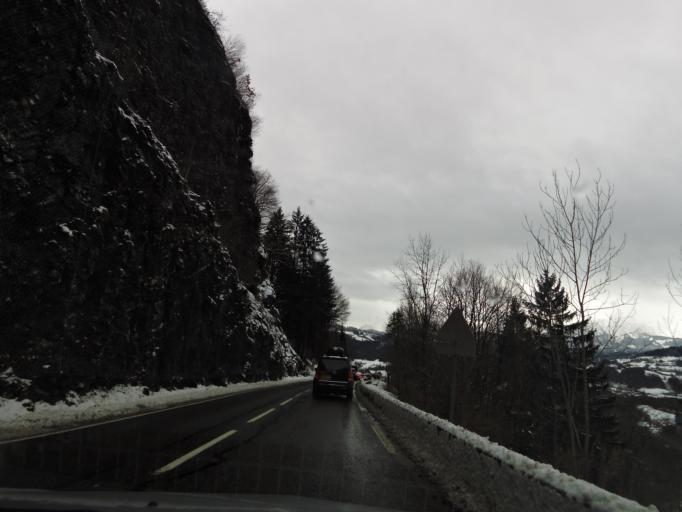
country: FR
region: Rhone-Alpes
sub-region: Departement de la Haute-Savoie
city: Taninges
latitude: 46.1161
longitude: 6.6029
